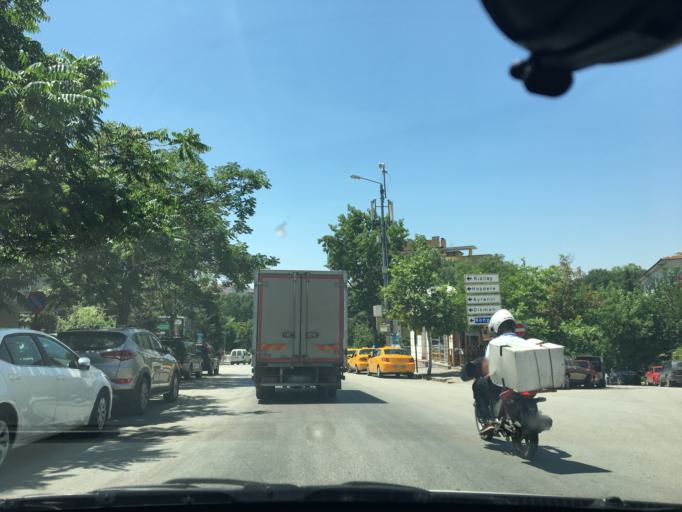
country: TR
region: Ankara
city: Ankara
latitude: 39.9078
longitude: 32.8546
